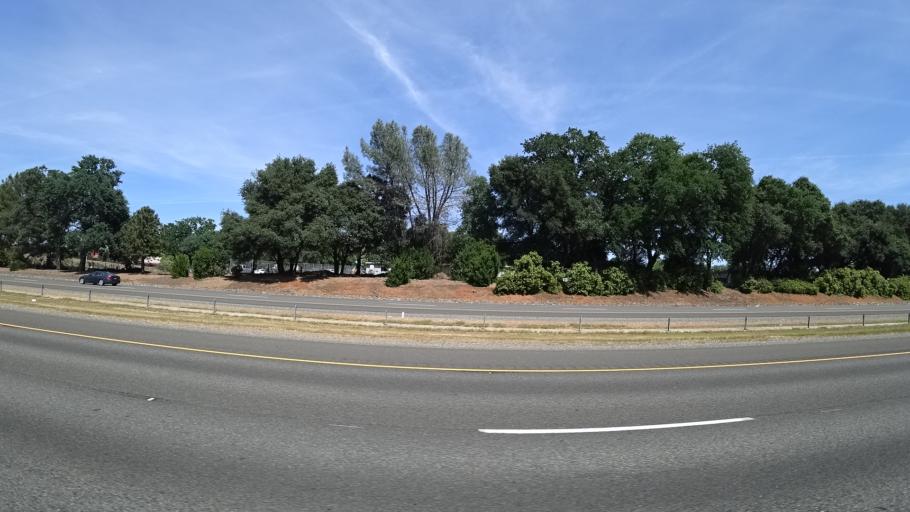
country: US
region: California
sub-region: Shasta County
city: Redding
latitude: 40.5629
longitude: -122.3590
